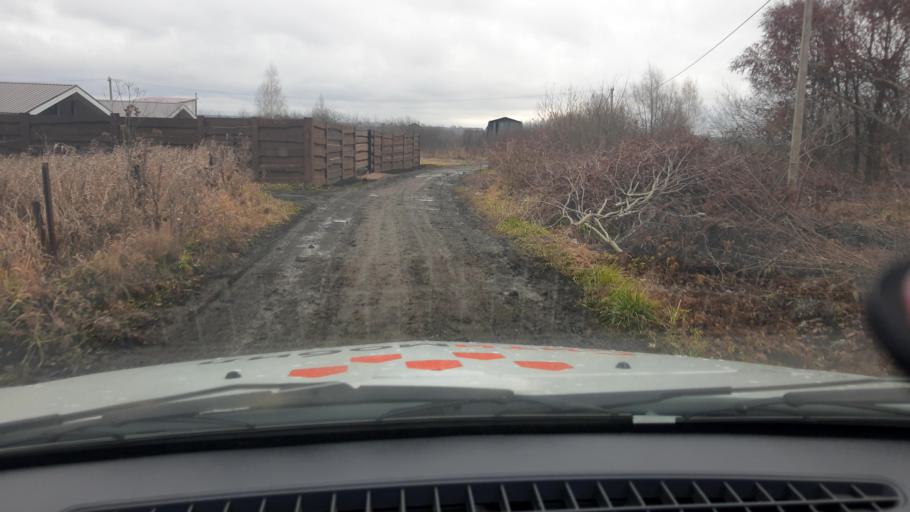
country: RU
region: Bashkortostan
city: Kabakovo
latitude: 54.7107
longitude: 56.1750
